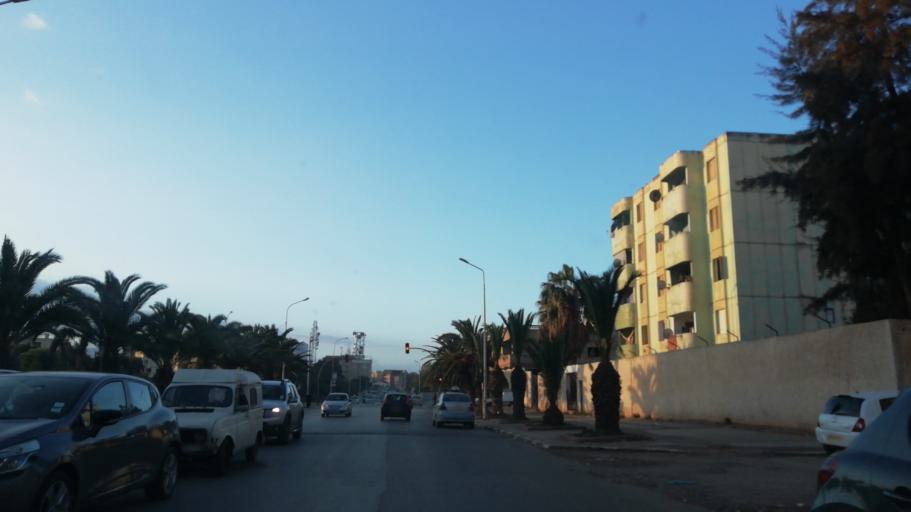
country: DZ
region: Oran
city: Oran
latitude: 35.6729
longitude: -0.6581
